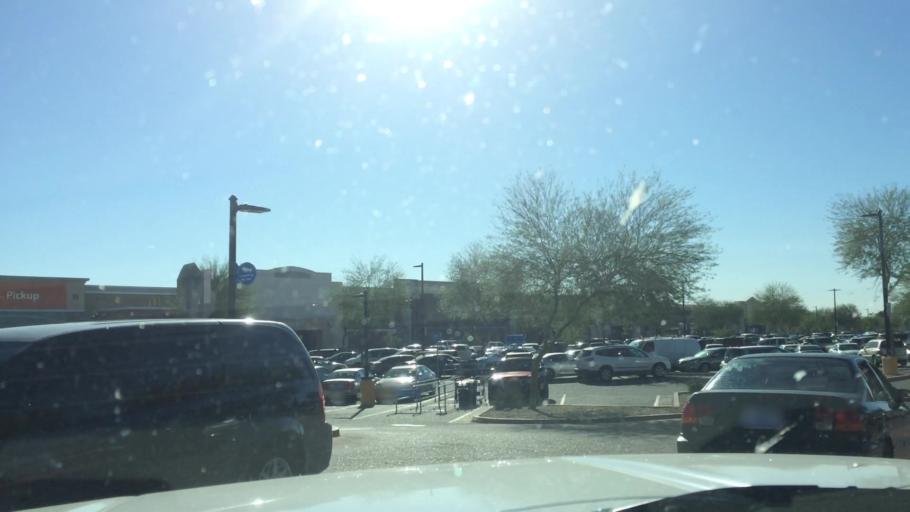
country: US
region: Arizona
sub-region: Maricopa County
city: Peoria
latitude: 33.5799
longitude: -112.2291
